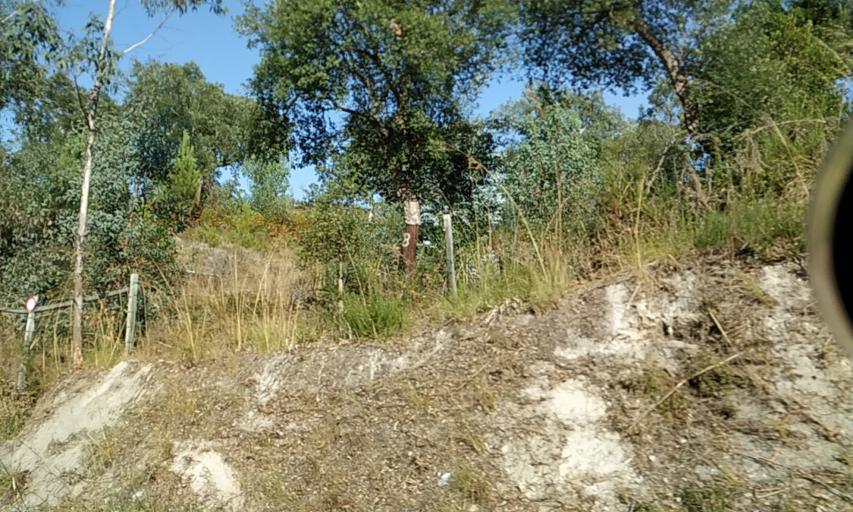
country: PT
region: Santarem
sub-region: Coruche
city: Coruche
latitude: 39.0610
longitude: -8.5660
